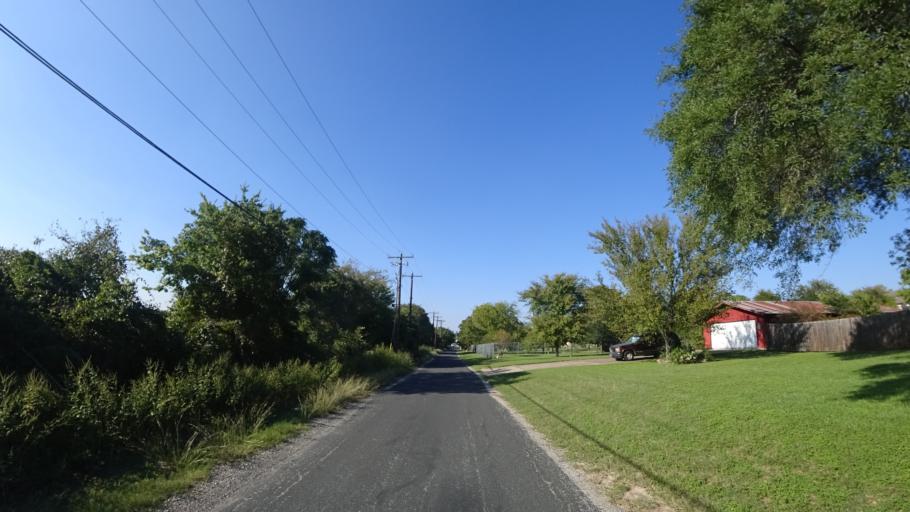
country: US
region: Texas
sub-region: Travis County
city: Austin
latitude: 30.3412
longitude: -97.6756
